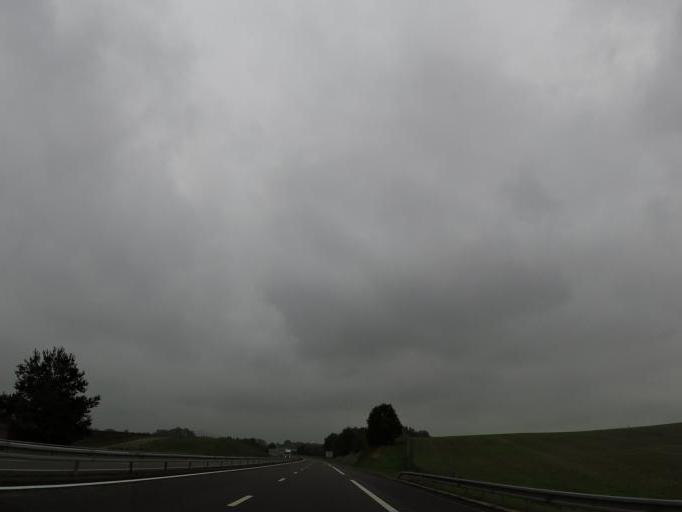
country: FR
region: Champagne-Ardenne
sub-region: Departement de la Marne
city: Sainte-Menehould
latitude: 49.0740
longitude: 4.8629
